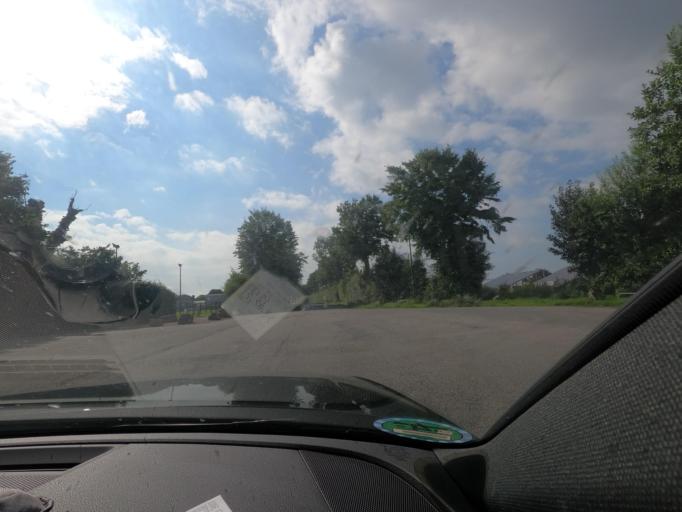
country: FR
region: Lower Normandy
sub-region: Departement du Calvados
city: La Riviere-Saint-Sauveur
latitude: 49.3936
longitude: 0.2546
